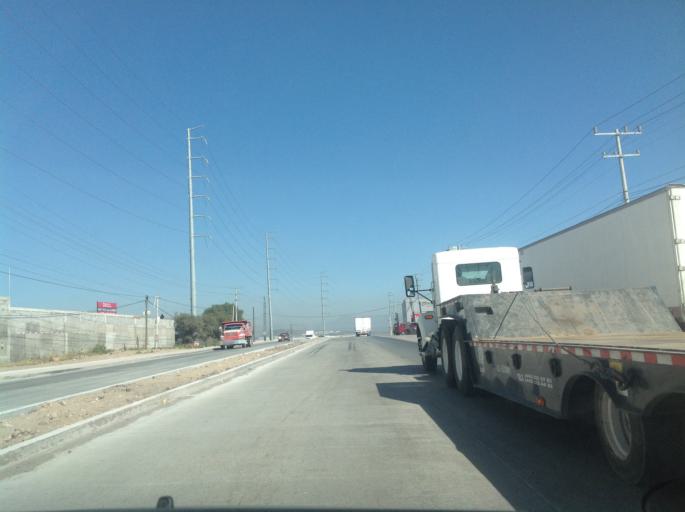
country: MX
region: Queretaro
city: El Colorado
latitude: 20.5626
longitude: -100.2677
